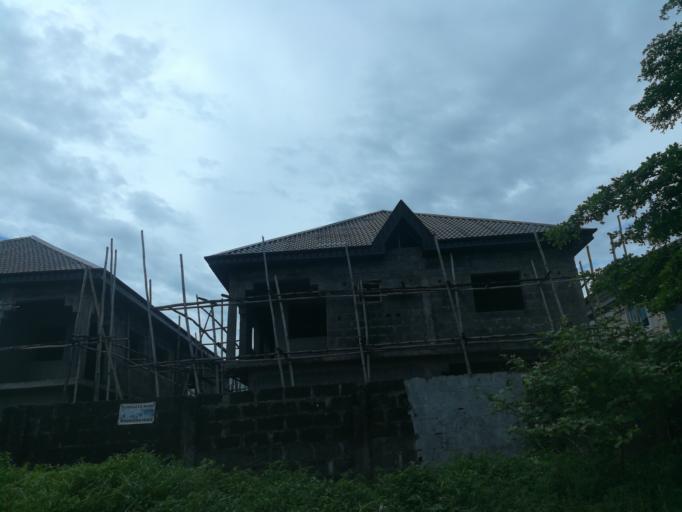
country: NG
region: Lagos
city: Ikoyi
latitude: 6.4412
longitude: 3.4777
